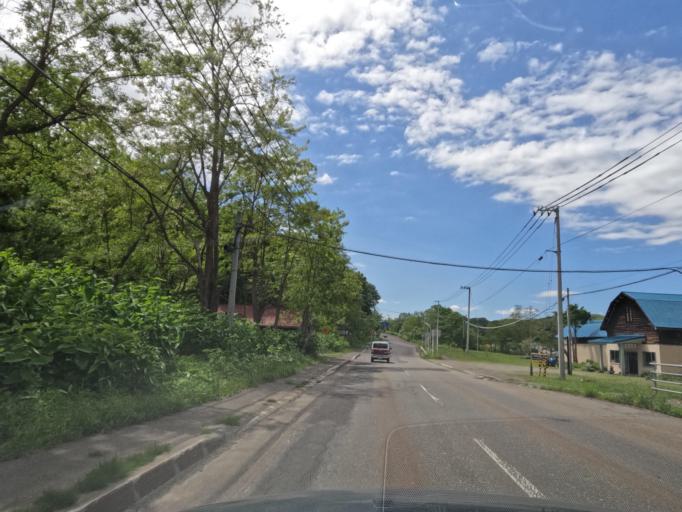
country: JP
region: Hokkaido
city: Bibai
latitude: 43.2535
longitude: 141.9212
